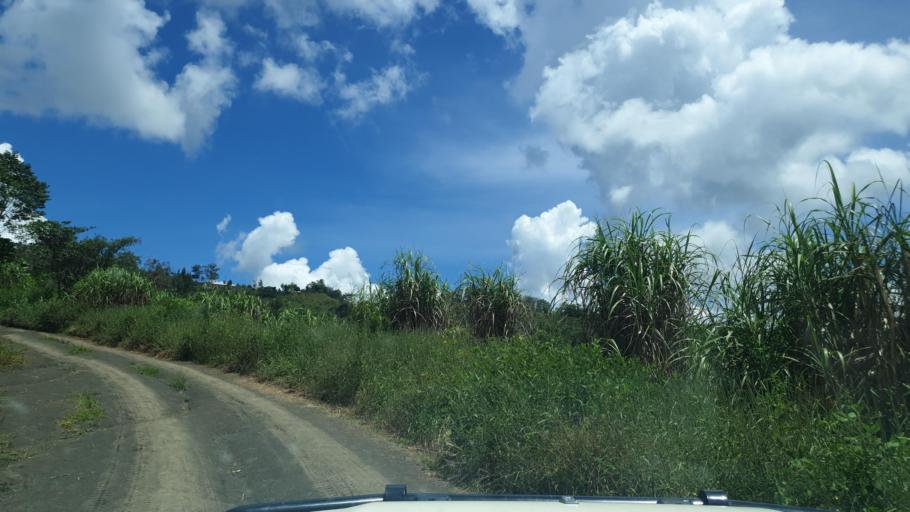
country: PG
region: Chimbu
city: Kundiawa
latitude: -6.2558
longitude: 145.1381
